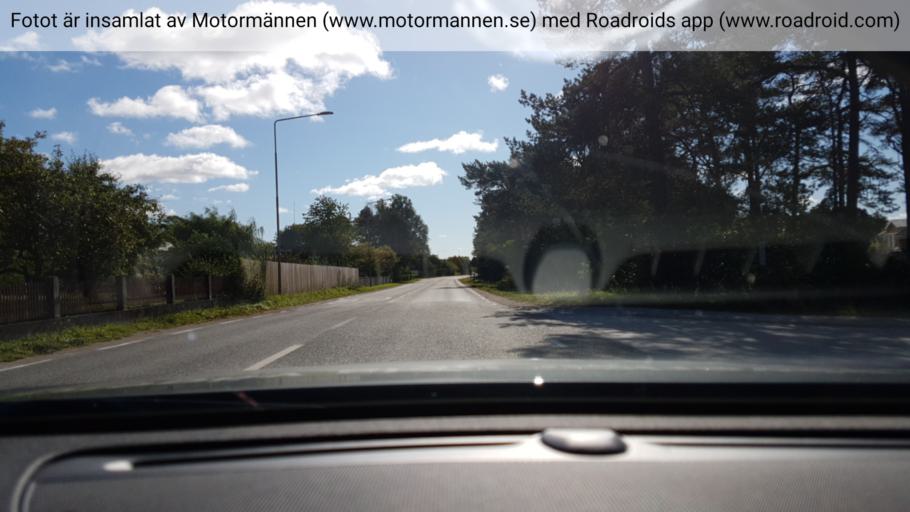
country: SE
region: Gotland
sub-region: Gotland
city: Slite
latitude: 57.7064
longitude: 18.7949
